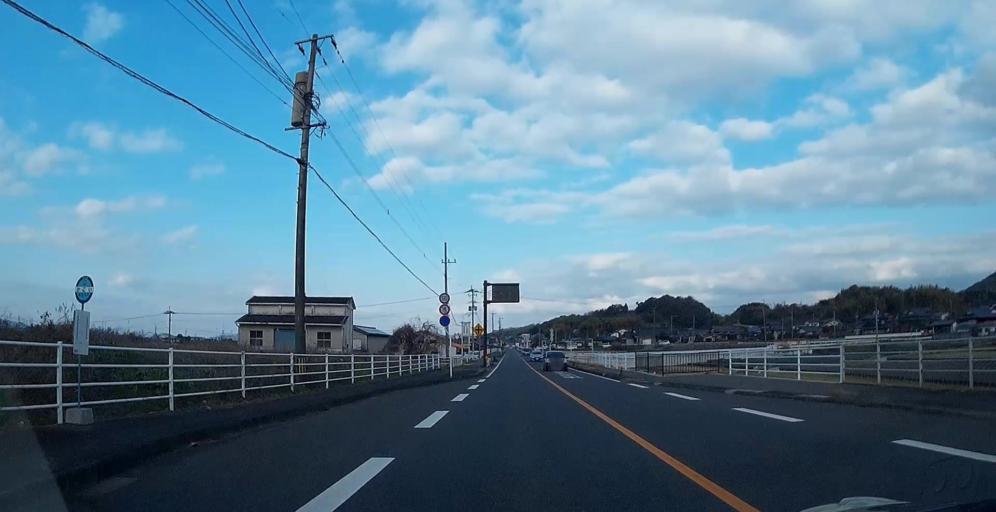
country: JP
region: Kumamoto
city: Yatsushiro
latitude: 32.5425
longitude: 130.6742
